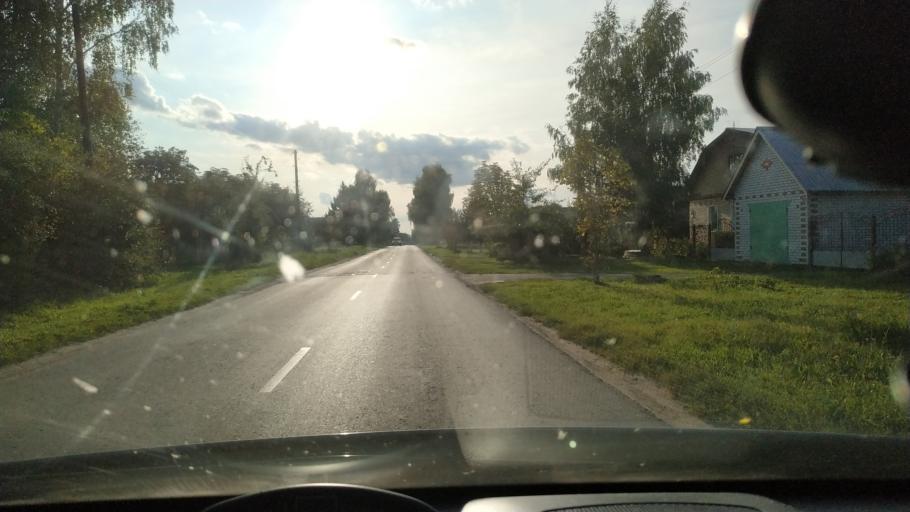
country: RU
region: Rjazan
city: Solotcha
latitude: 54.8665
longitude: 39.6632
